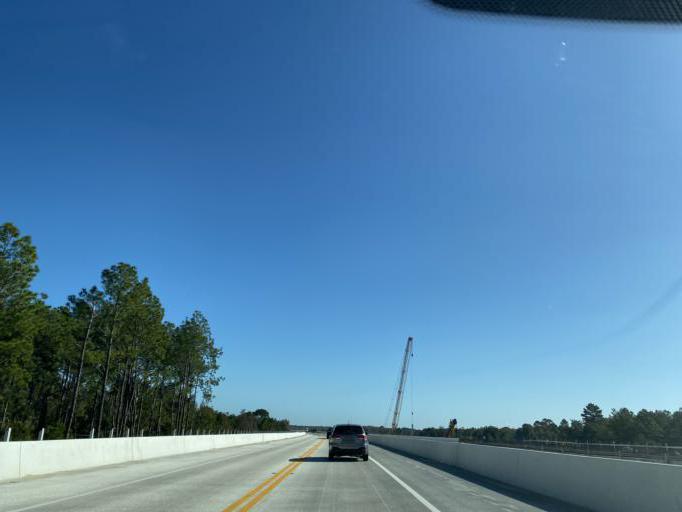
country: US
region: Florida
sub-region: Lake County
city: Mount Plymouth
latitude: 28.8117
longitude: -81.4557
